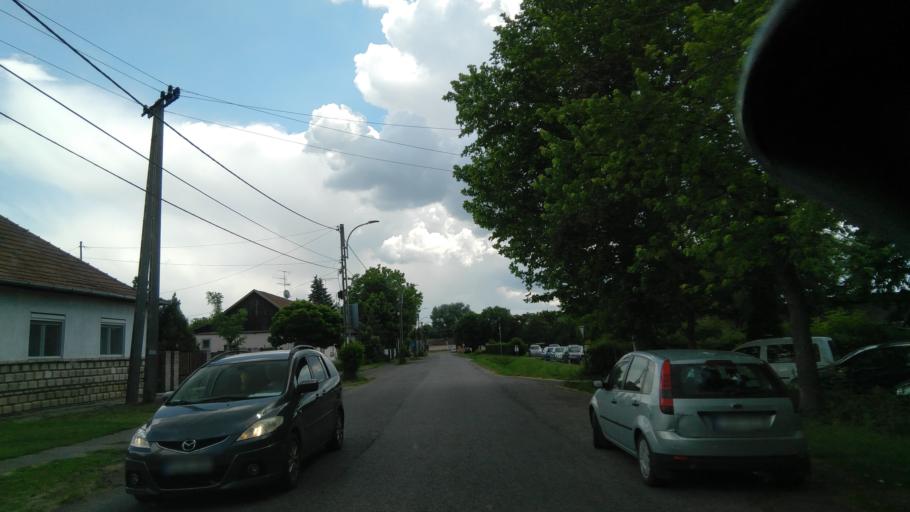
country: HU
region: Bekes
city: Gyula
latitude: 46.6589
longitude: 21.2695
